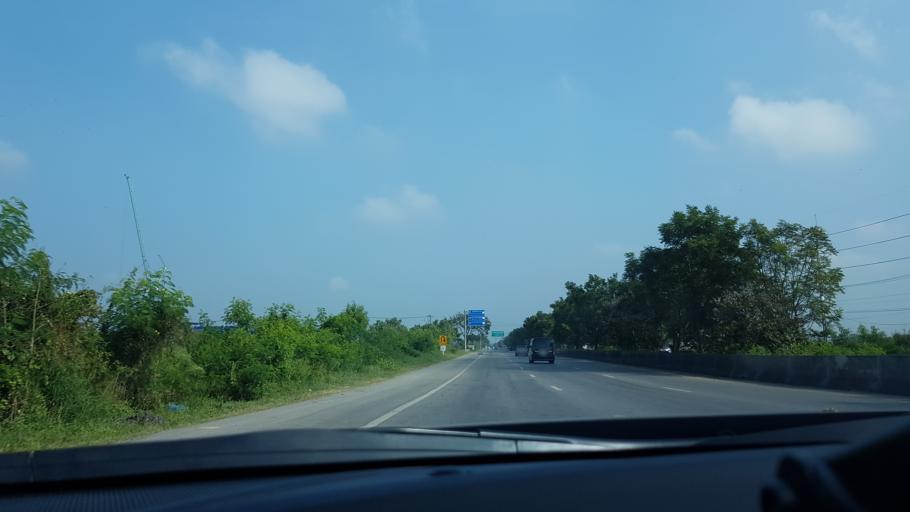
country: TH
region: Pathum Thani
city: Sam Khok
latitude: 14.1344
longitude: 100.5694
